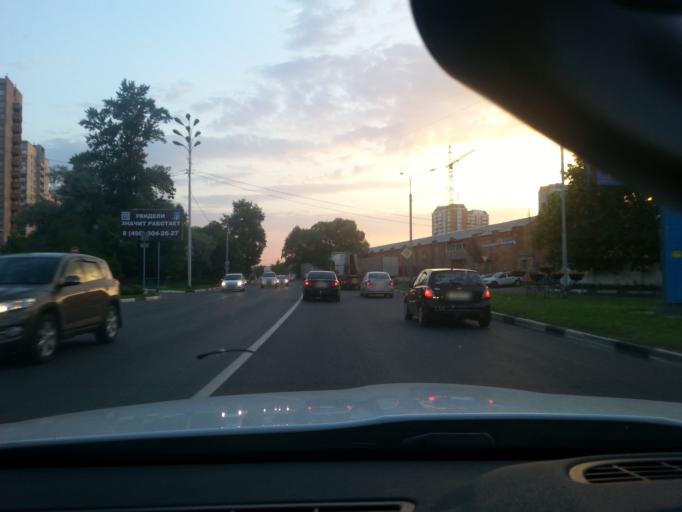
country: RU
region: Moskovskaya
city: Zheleznodorozhnyy
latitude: 55.7514
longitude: 38.0048
